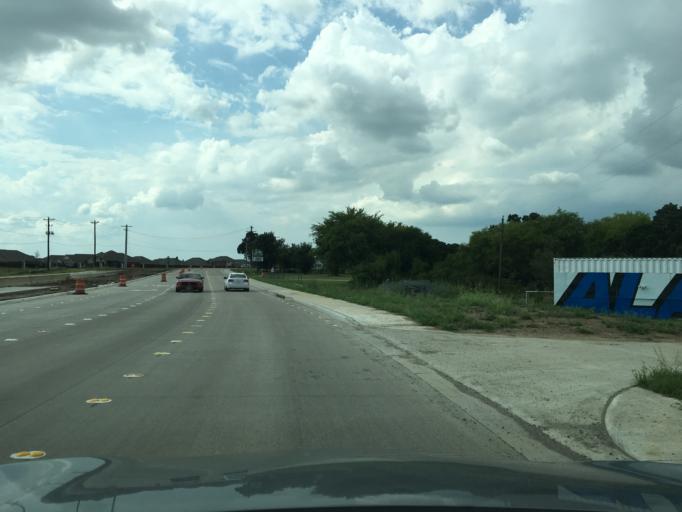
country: US
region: Texas
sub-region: Denton County
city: Oak Point
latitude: 33.1960
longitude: -96.9770
